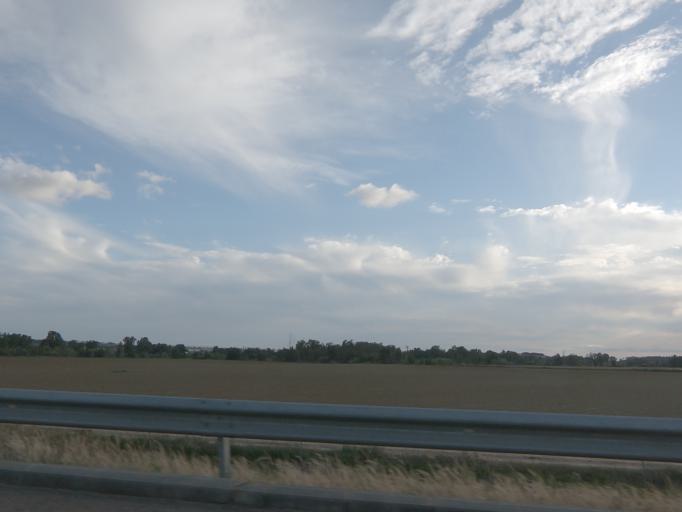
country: ES
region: Extremadura
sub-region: Provincia de Badajoz
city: Badajoz
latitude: 38.9034
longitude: -6.9319
